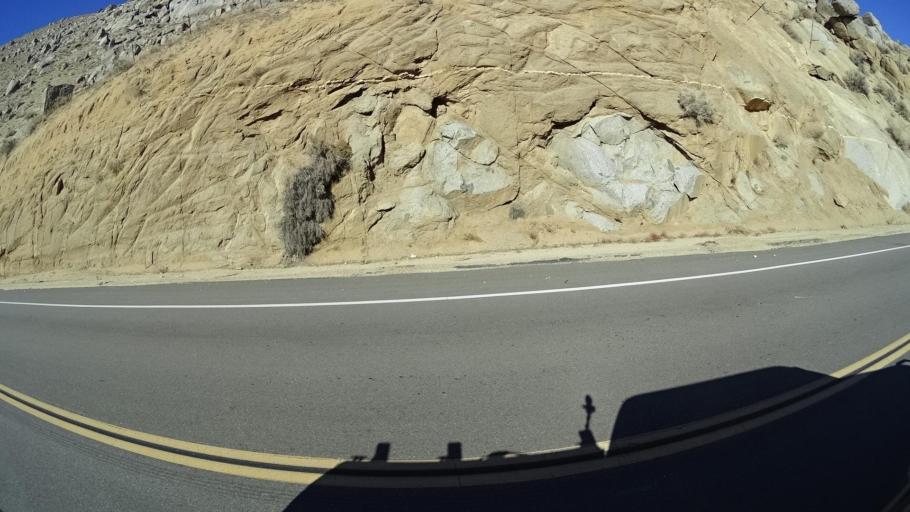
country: US
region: California
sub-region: Kern County
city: Weldon
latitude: 35.6733
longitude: -118.3300
